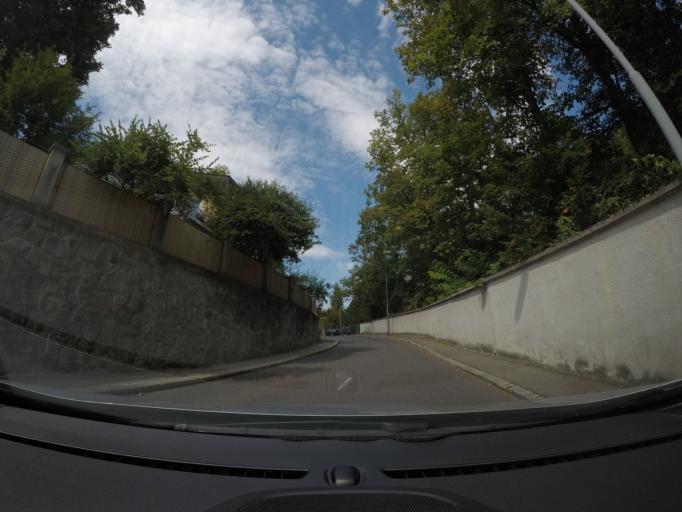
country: AT
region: Lower Austria
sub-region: Politischer Bezirk Modling
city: Perchtoldsdorf
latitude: 48.1886
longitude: 16.2638
